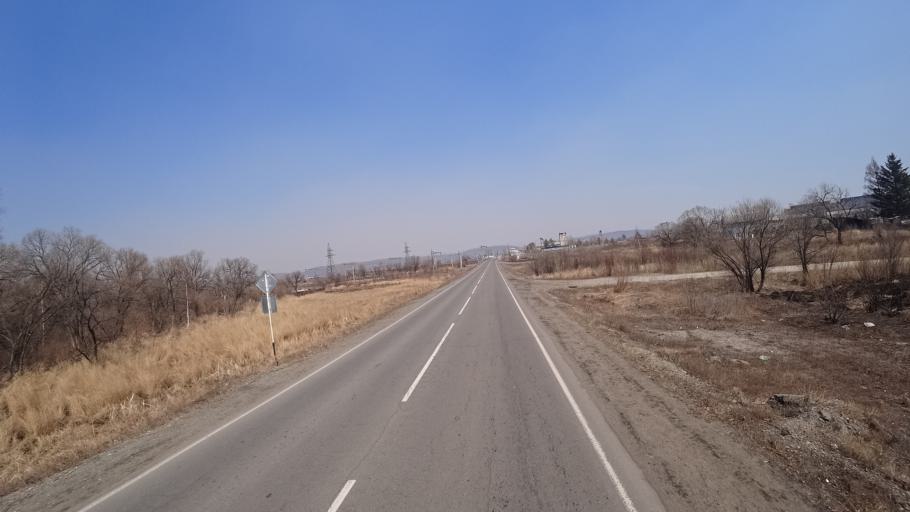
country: RU
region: Amur
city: Novobureyskiy
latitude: 49.7906
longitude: 129.8502
